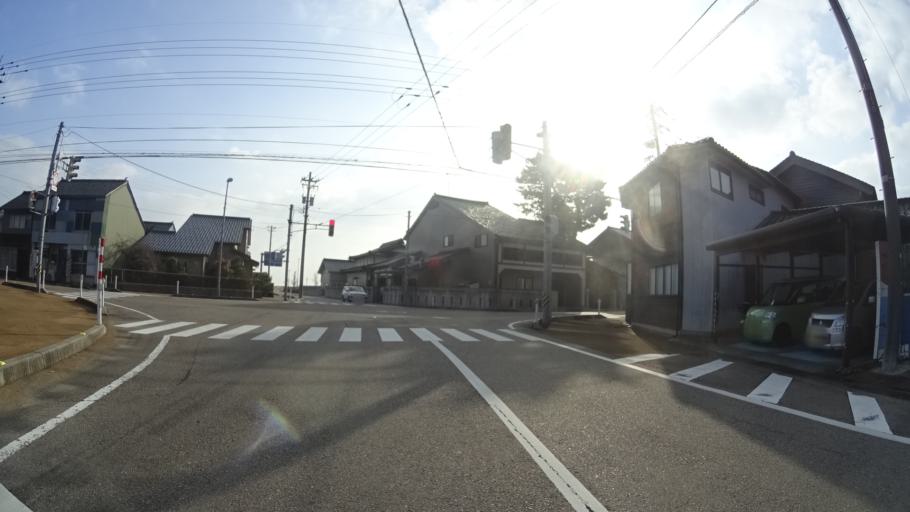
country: JP
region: Toyama
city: Himi
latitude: 36.8719
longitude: 136.9828
